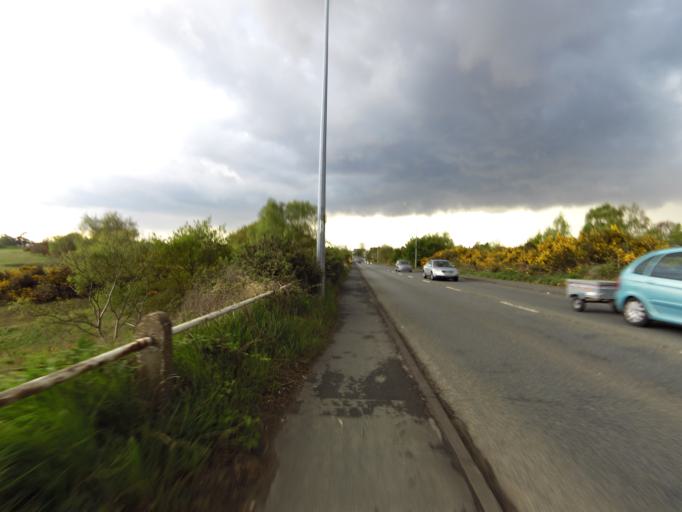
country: GB
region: England
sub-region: Suffolk
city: Kesgrave
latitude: 52.0624
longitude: 1.2084
